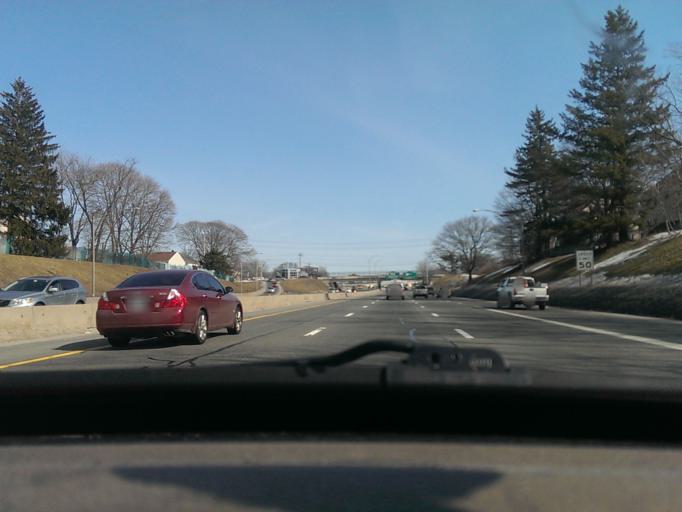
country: US
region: Rhode Island
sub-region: Providence County
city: East Providence
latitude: 41.8130
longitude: -71.3624
